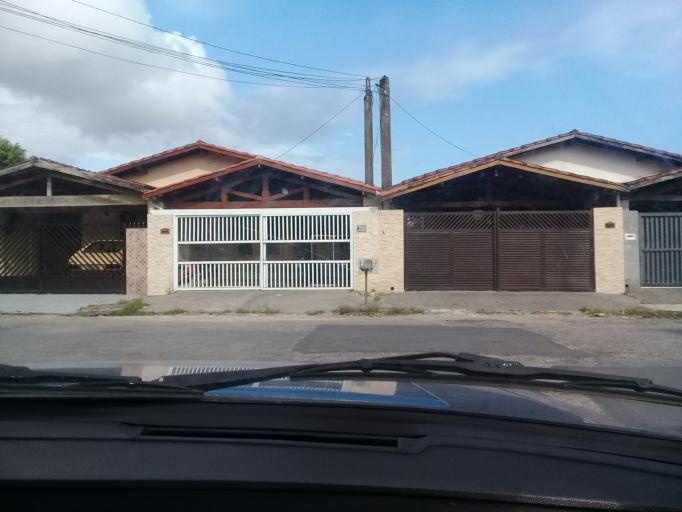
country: BR
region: Sao Paulo
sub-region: Guaruja
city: Guaruja
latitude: -23.9885
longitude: -46.2794
